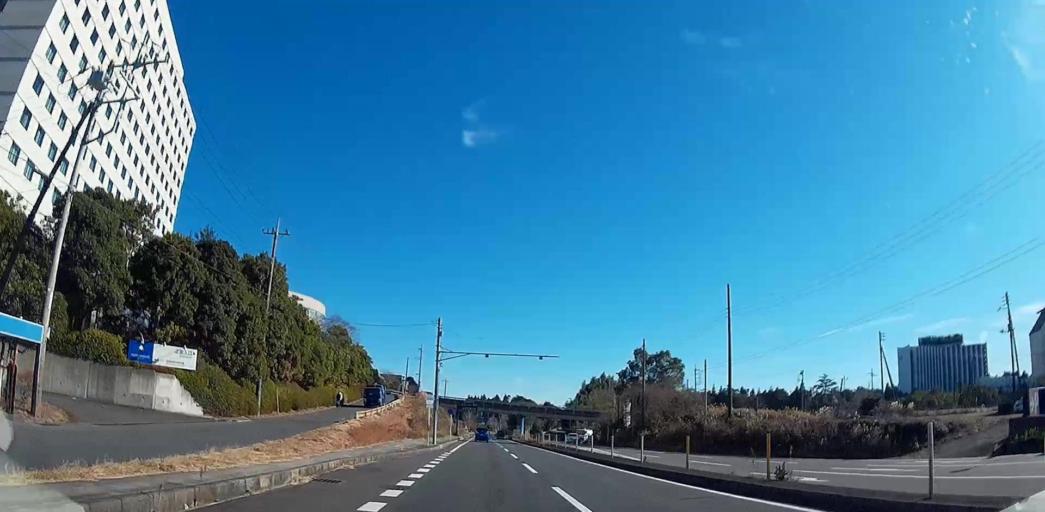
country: JP
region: Chiba
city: Narita
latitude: 35.7832
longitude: 140.3508
